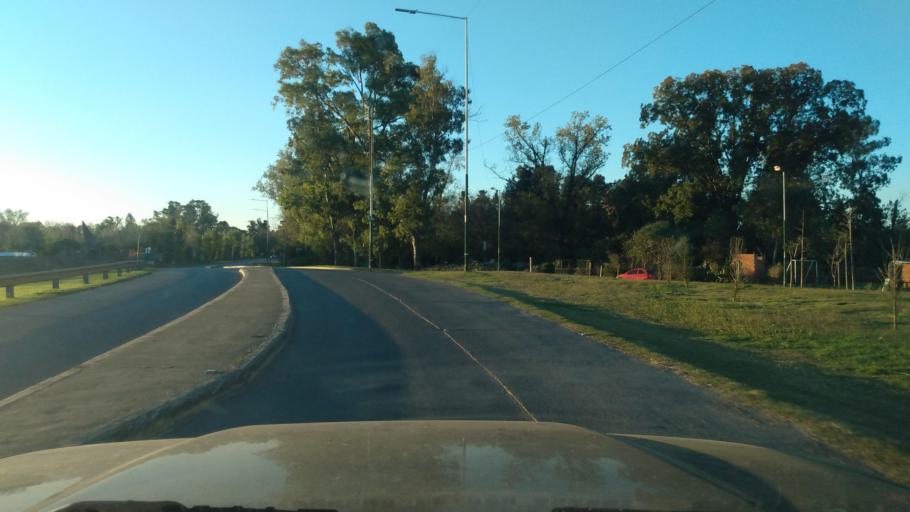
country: AR
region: Buenos Aires
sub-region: Partido de Merlo
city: Merlo
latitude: -34.6411
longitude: -58.7309
